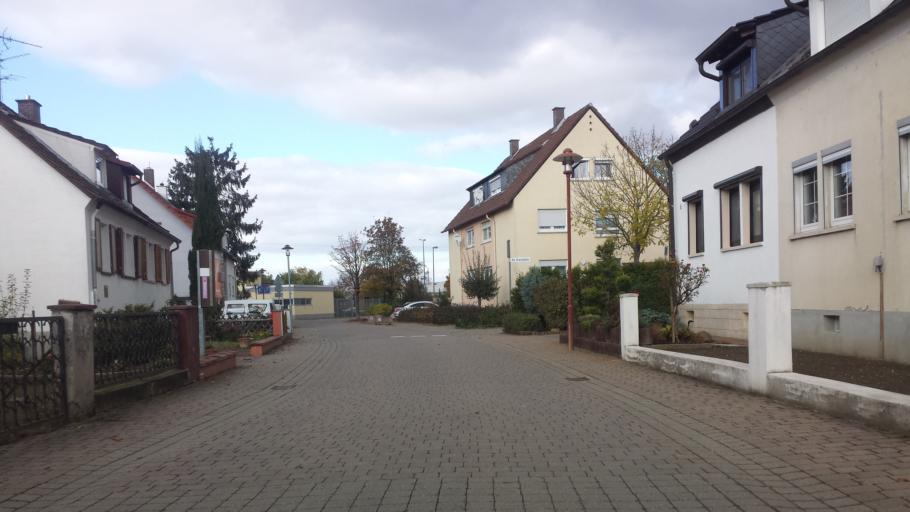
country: DE
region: Rheinland-Pfalz
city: Fussgonheim
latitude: 49.4642
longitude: 8.2932
